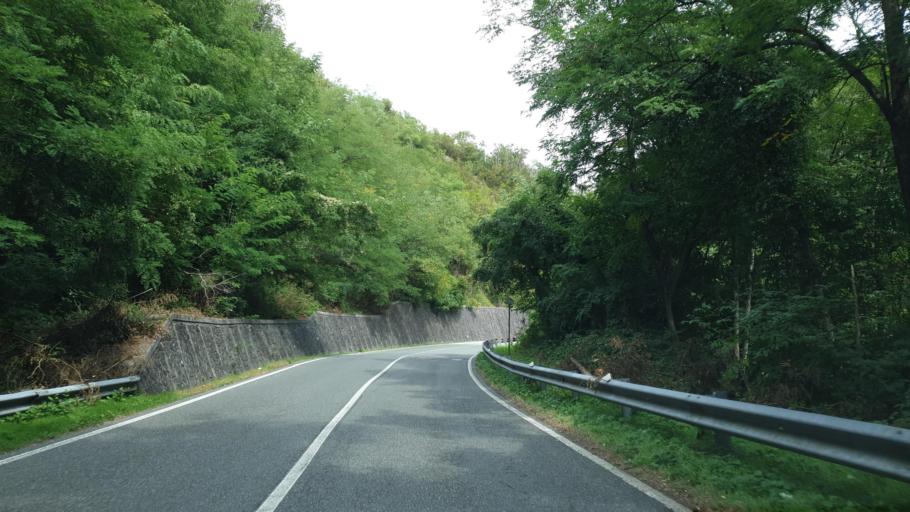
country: IT
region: Liguria
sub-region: Provincia di La Spezia
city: Carrodano
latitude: 44.2156
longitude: 9.6277
